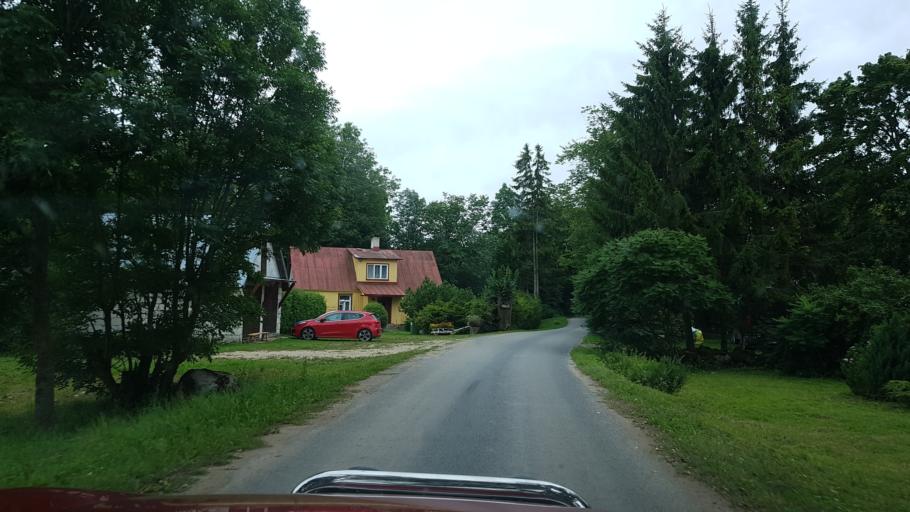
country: EE
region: Laeaene
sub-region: Ridala Parish
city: Uuemoisa
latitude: 58.7891
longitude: 23.6627
